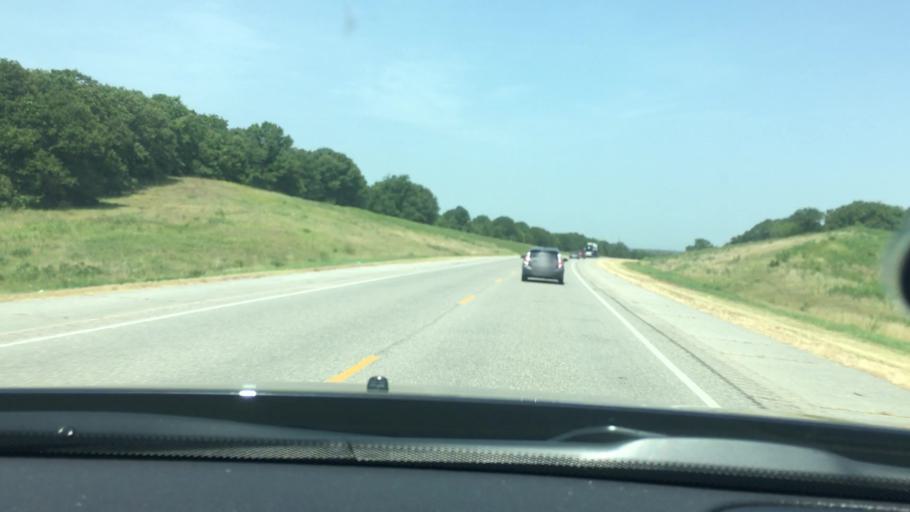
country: US
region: Oklahoma
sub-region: Coal County
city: Coalgate
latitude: 34.6007
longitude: -96.3645
